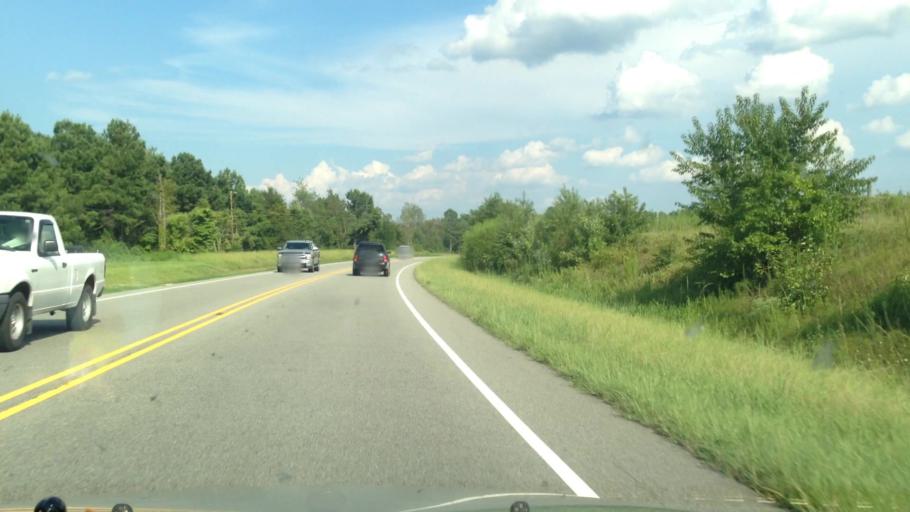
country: US
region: North Carolina
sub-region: Harnett County
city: Lillington
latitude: 35.4183
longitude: -78.8791
